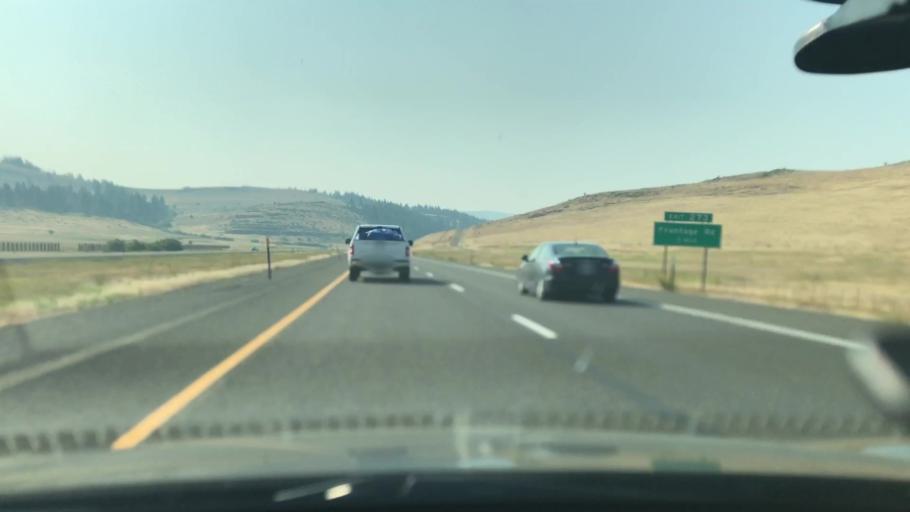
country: US
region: Oregon
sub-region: Union County
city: Union
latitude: 45.1712
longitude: -117.9694
